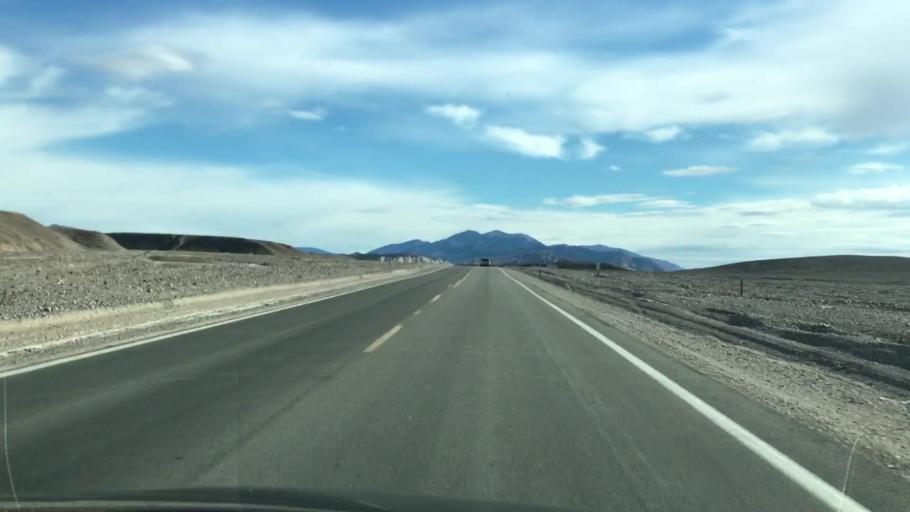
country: US
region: Nevada
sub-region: Nye County
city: Beatty
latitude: 36.4942
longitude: -116.8724
